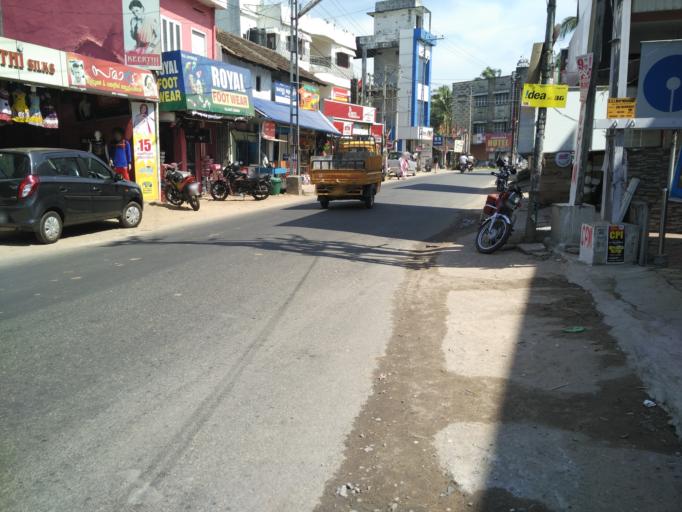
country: IN
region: Kerala
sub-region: Palakkad district
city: Chittur
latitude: 10.5944
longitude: 76.6014
